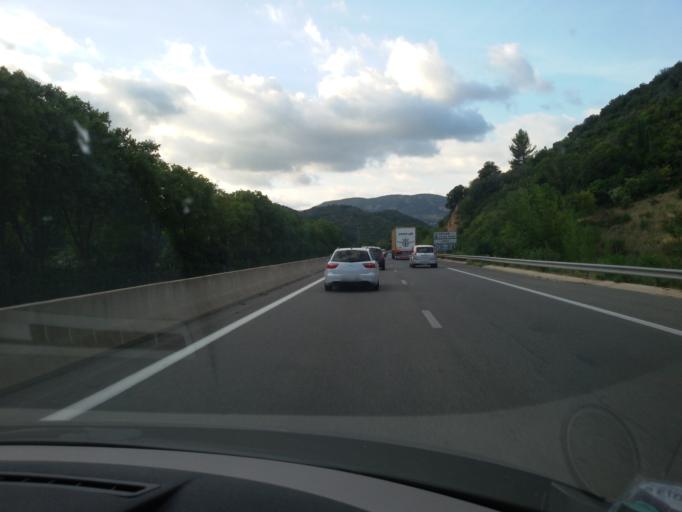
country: FR
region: Languedoc-Roussillon
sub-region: Departement de l'Herault
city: Lodeve
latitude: 43.7079
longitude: 3.3268
